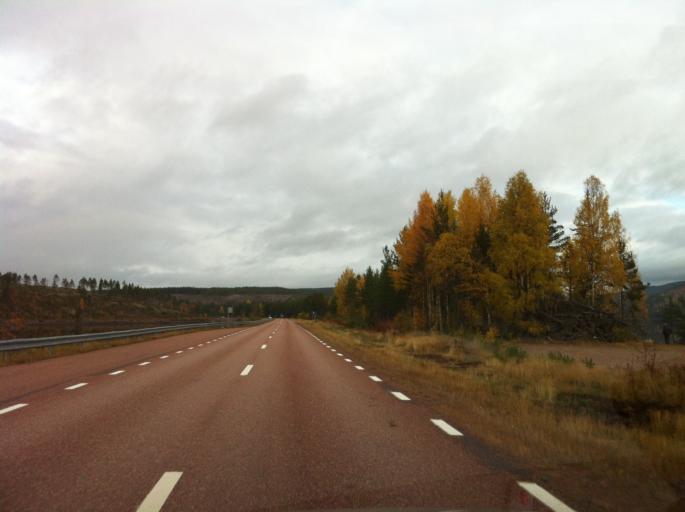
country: SE
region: Dalarna
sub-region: Alvdalens Kommun
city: AElvdalen
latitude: 61.3000
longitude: 13.7287
